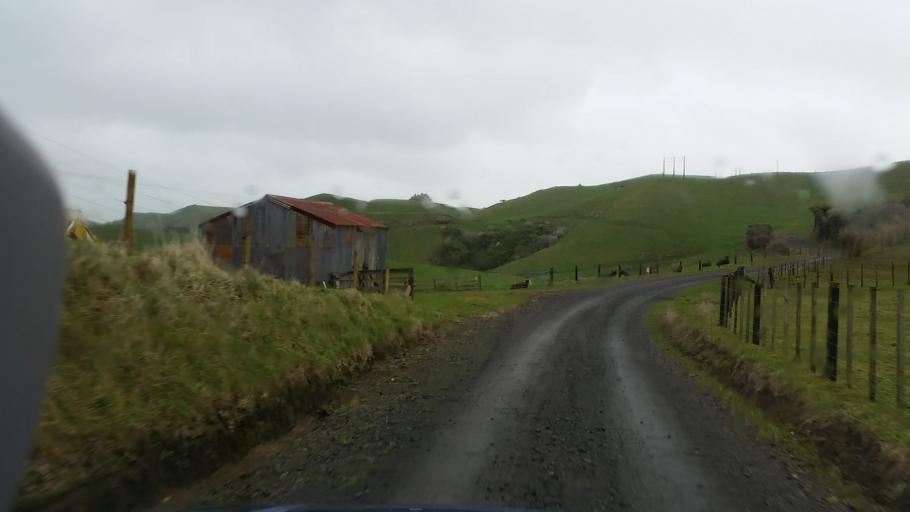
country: NZ
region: Taranaki
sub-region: South Taranaki District
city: Eltham
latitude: -39.2784
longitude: 174.3384
